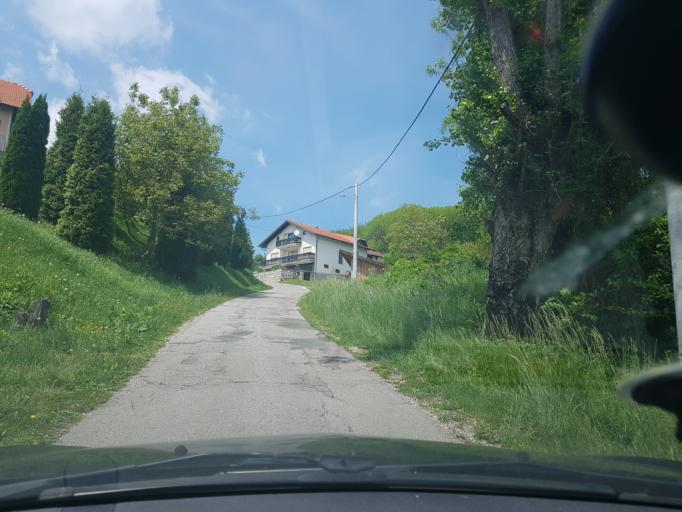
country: SI
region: Rogatec
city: Rogatec
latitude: 46.2129
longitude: 15.7186
